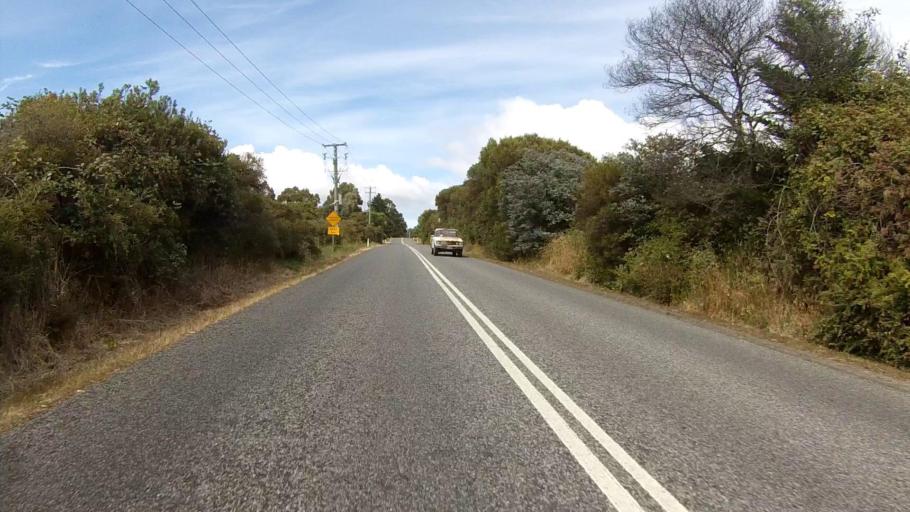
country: AU
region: Tasmania
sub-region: Kingborough
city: Kettering
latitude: -43.1365
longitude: 147.2467
